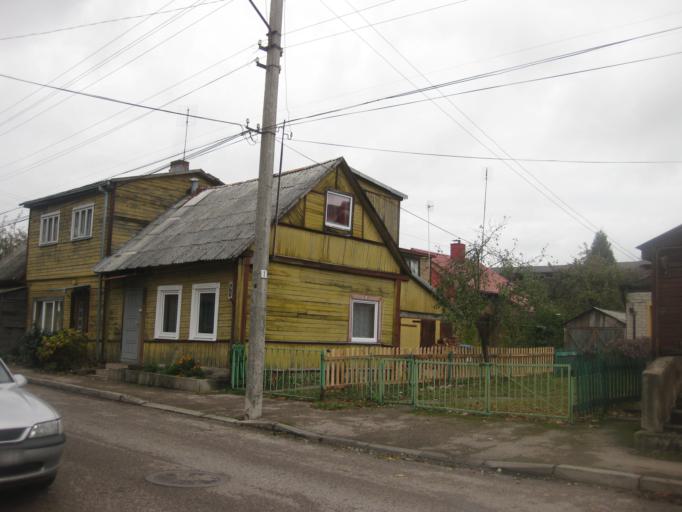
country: LT
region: Kauno apskritis
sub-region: Kaunas
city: Kaunas
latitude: 54.9073
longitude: 23.9238
